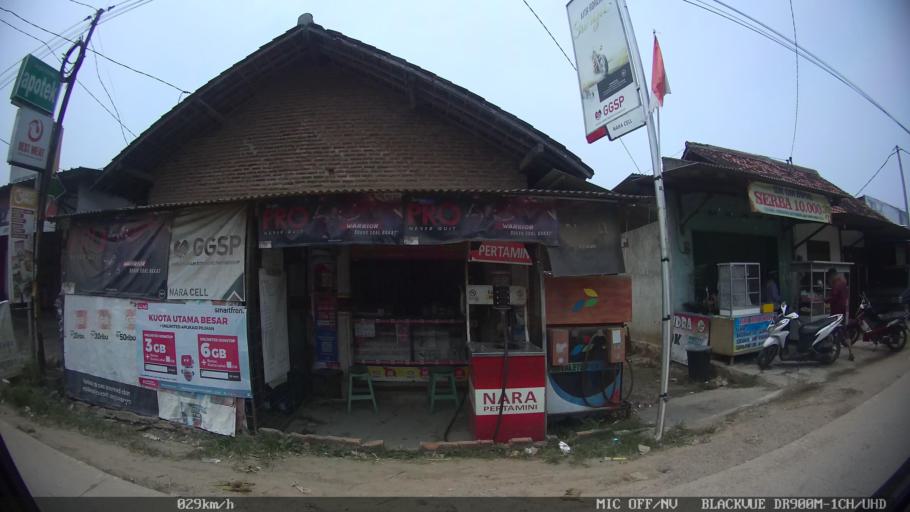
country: ID
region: Lampung
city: Bandarlampung
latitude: -5.4073
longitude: 105.2980
